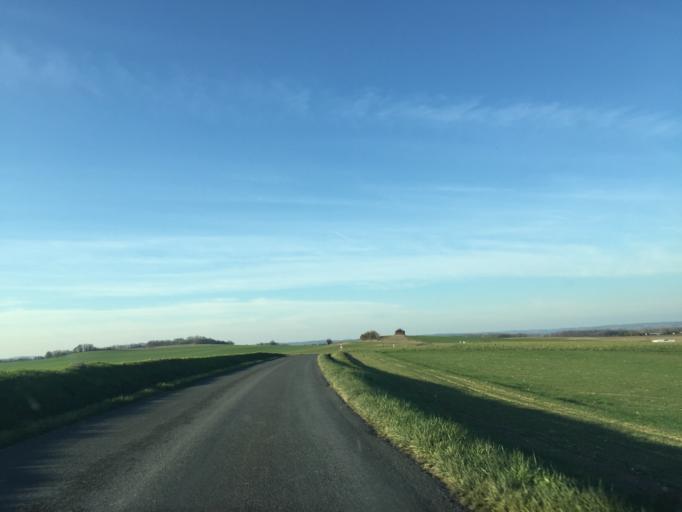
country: FR
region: Aquitaine
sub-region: Departement de la Dordogne
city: Riberac
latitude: 45.2294
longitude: 0.2657
